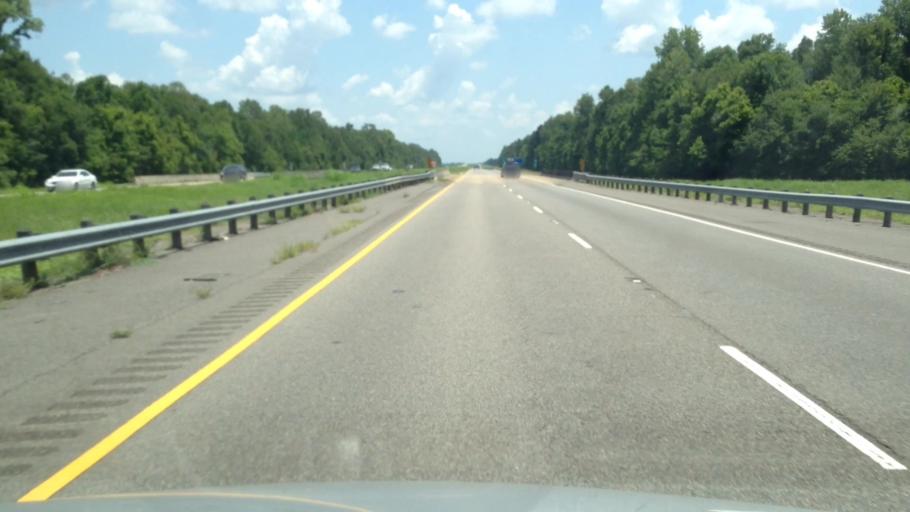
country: US
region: Louisiana
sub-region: Avoyelles Parish
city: Bunkie
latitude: 30.9672
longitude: -92.2889
